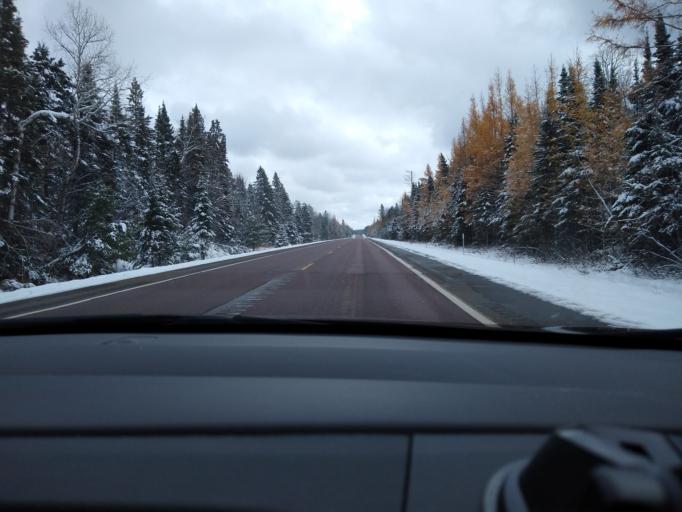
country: US
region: Michigan
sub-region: Iron County
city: Iron River
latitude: 46.1680
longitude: -88.9222
